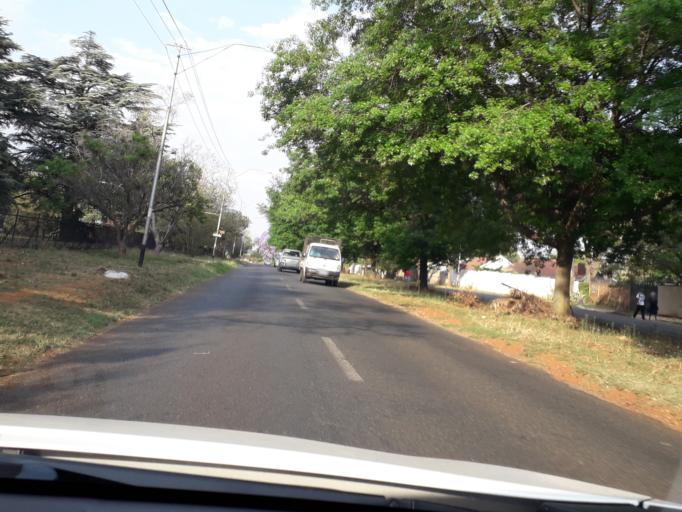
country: ZA
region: Gauteng
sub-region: City of Johannesburg Metropolitan Municipality
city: Johannesburg
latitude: -26.1619
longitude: 27.9852
